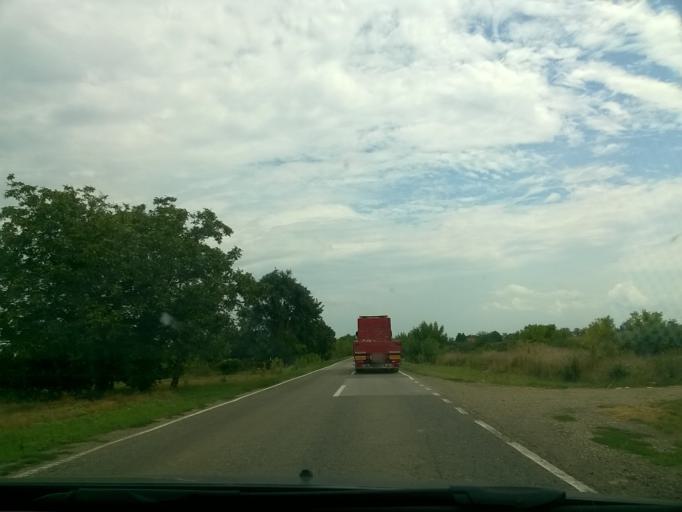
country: RS
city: Klek
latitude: 45.3862
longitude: 20.4800
